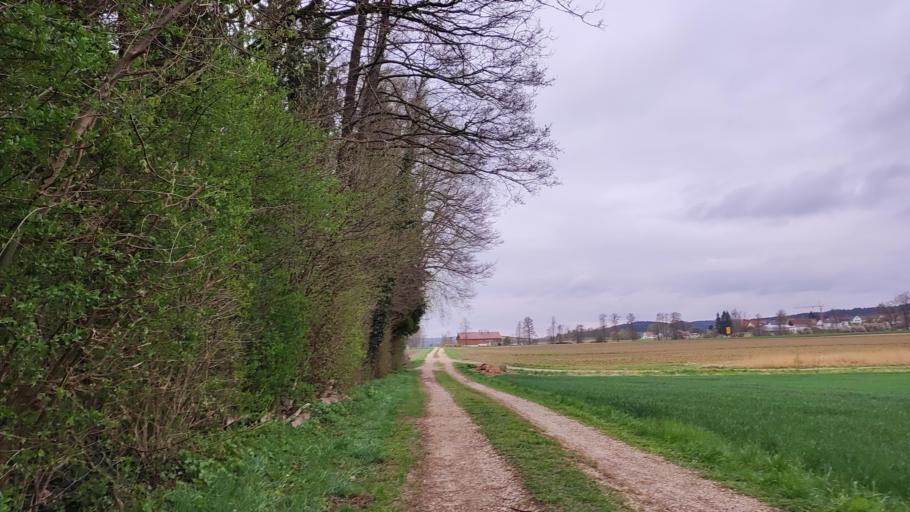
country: DE
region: Bavaria
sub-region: Swabia
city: Altenmunster
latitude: 48.4520
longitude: 10.5923
